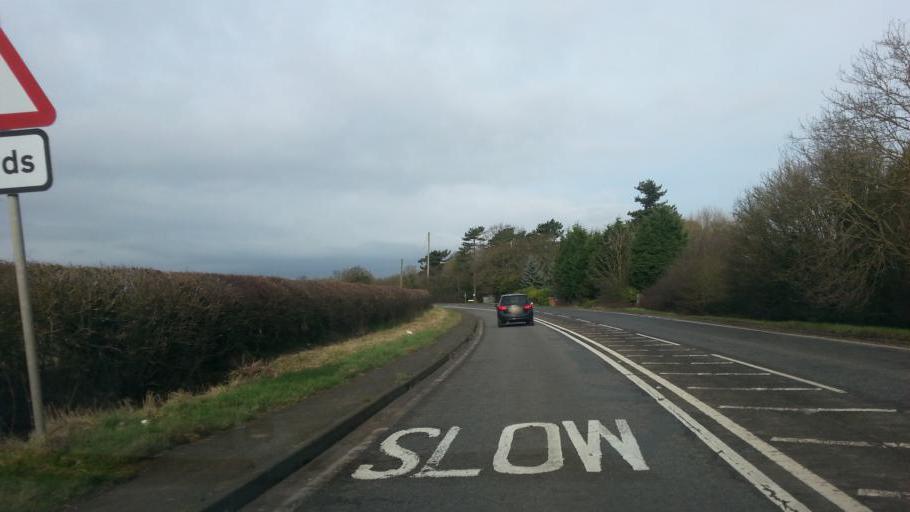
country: GB
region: England
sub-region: Nottinghamshire
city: Cotgrave
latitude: 52.8798
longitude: -1.0582
